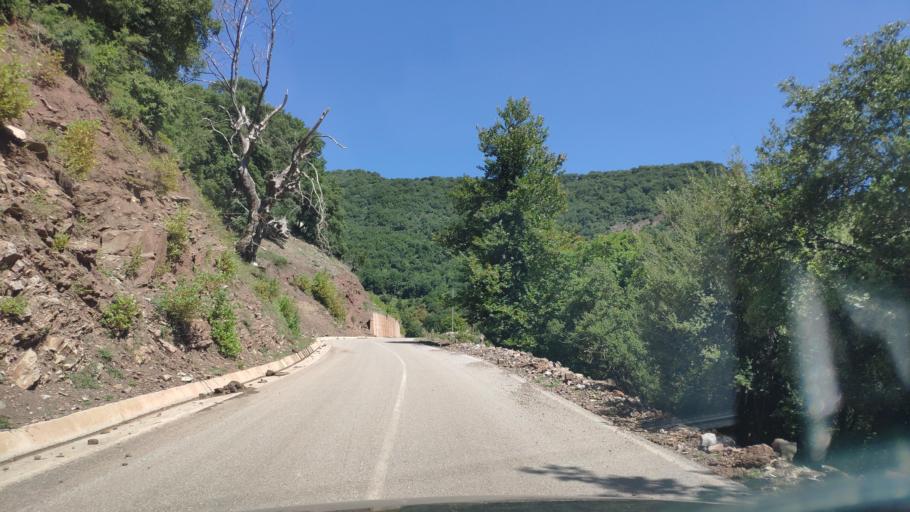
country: GR
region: Central Greece
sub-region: Nomos Evrytanias
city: Kerasochori
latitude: 39.0874
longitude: 21.5965
